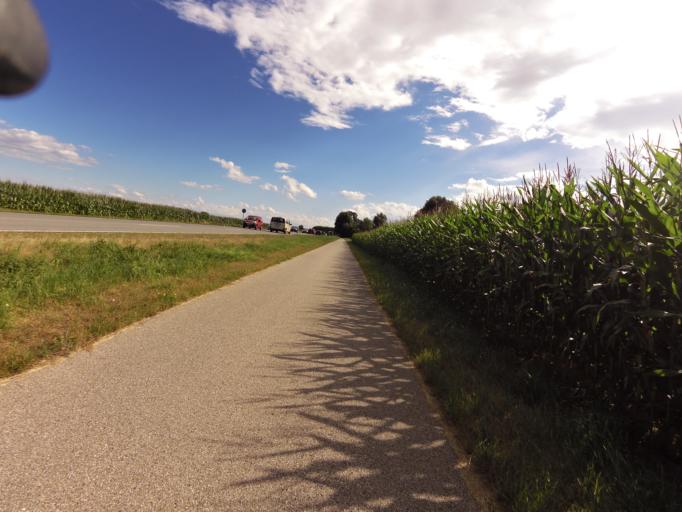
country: DE
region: Bavaria
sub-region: Upper Bavaria
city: Hallbergmoos
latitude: 48.3456
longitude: 11.7357
